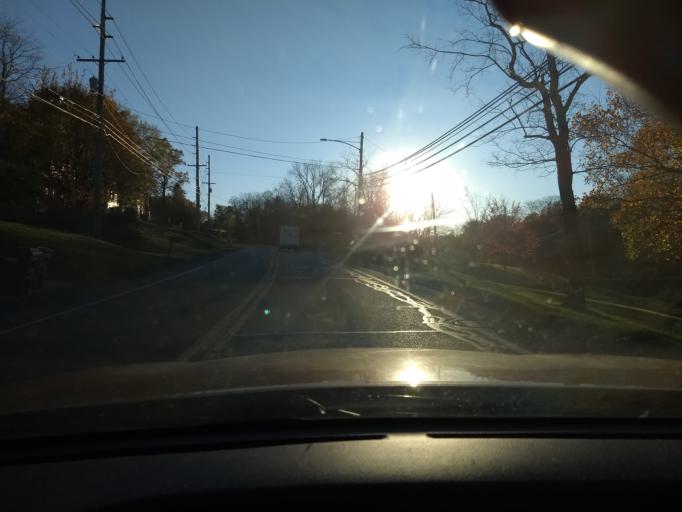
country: US
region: Pennsylvania
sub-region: Allegheny County
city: Upper Saint Clair
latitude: 40.3239
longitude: -80.0674
